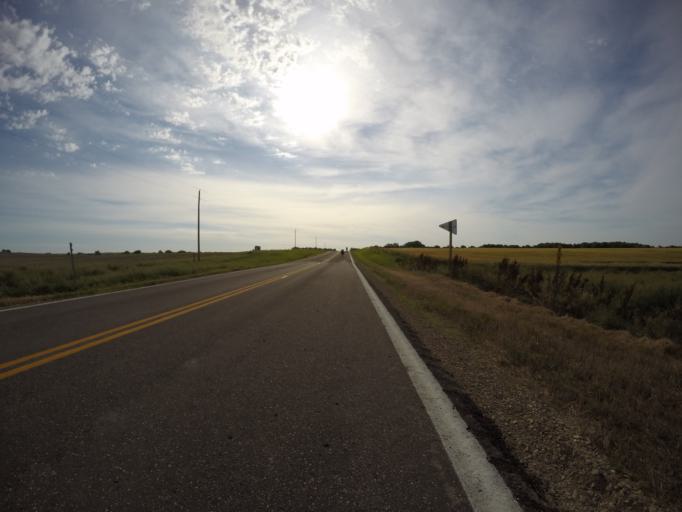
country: US
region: Kansas
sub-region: Republic County
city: Belleville
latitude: 39.7120
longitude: -97.4119
